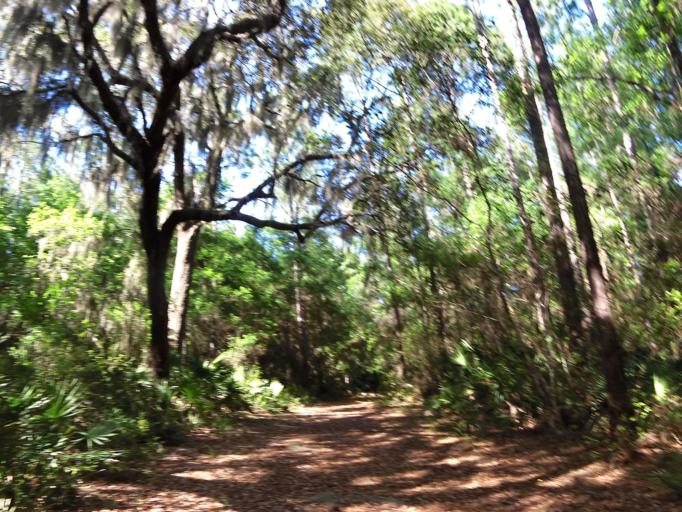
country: US
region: Florida
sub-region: Duval County
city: Atlantic Beach
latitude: 30.4529
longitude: -81.4818
